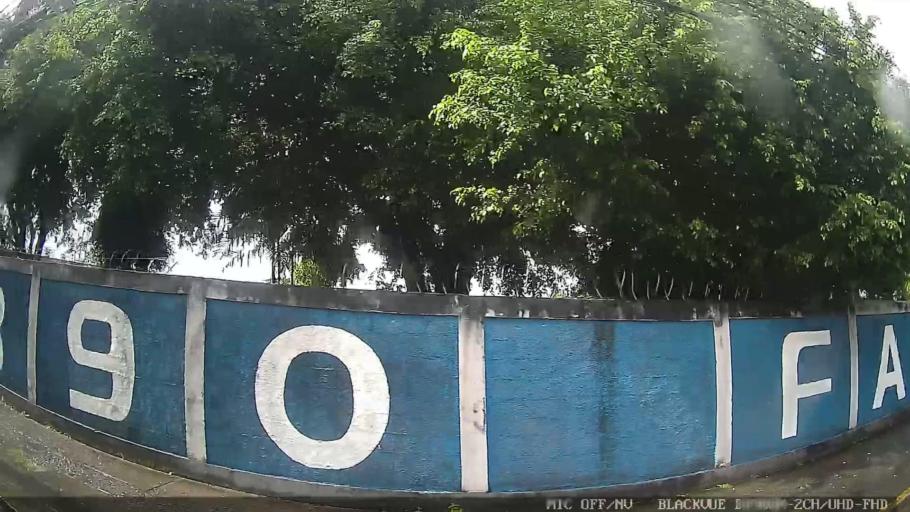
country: BR
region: Sao Paulo
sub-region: Itanhaem
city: Itanhaem
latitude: -24.1829
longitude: -46.8181
